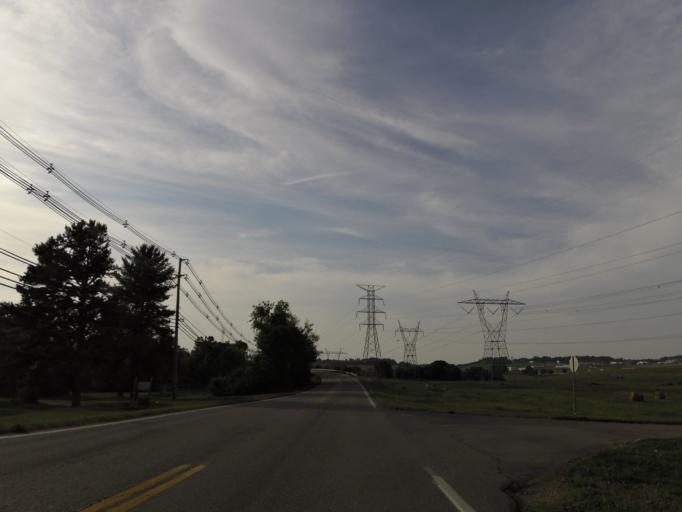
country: US
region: Tennessee
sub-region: Blount County
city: Alcoa
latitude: 35.7911
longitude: -84.0123
